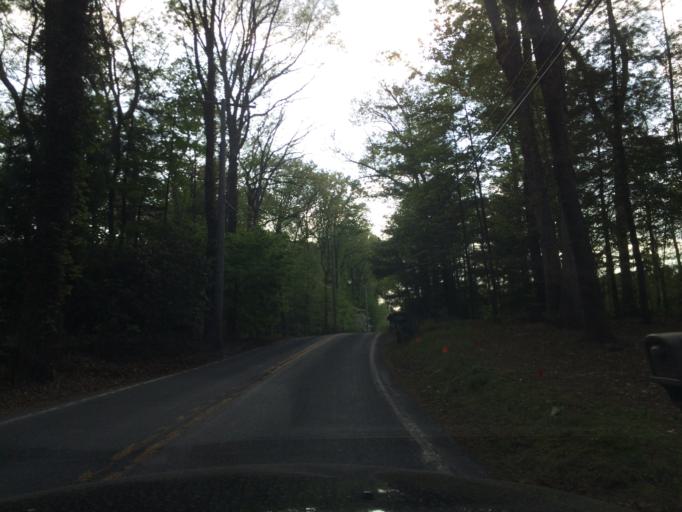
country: US
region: Maryland
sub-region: Carroll County
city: Mount Airy
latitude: 39.2934
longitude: -77.0771
